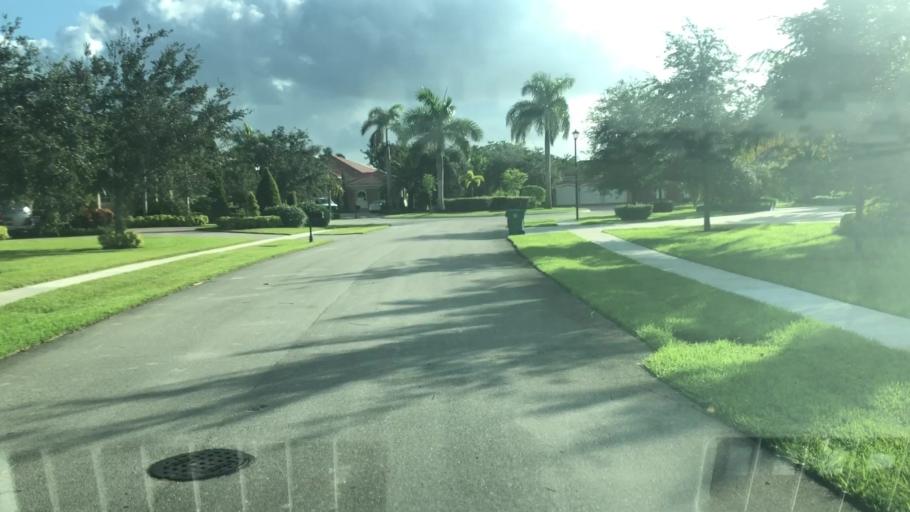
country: US
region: Florida
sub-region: Broward County
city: Cooper City
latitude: 26.0658
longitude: -80.2954
